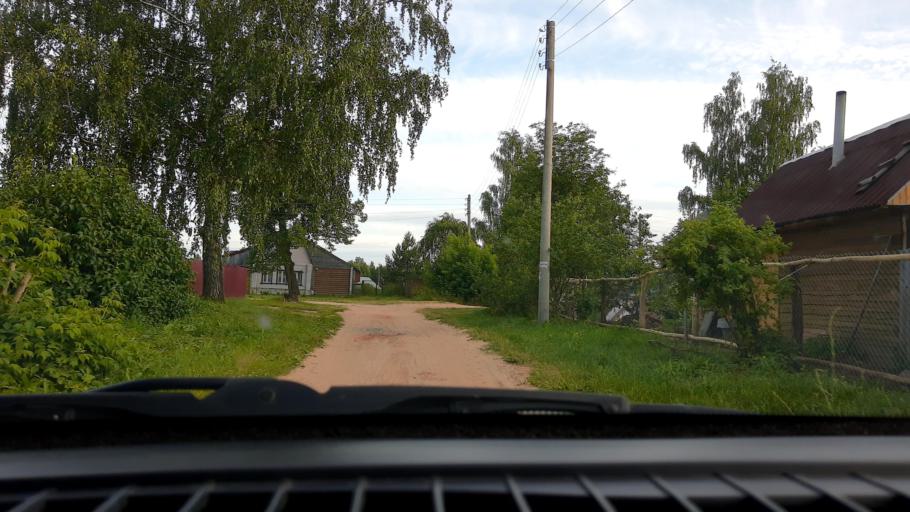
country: RU
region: Nizjnij Novgorod
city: Kstovo
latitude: 56.2650
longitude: 44.3013
